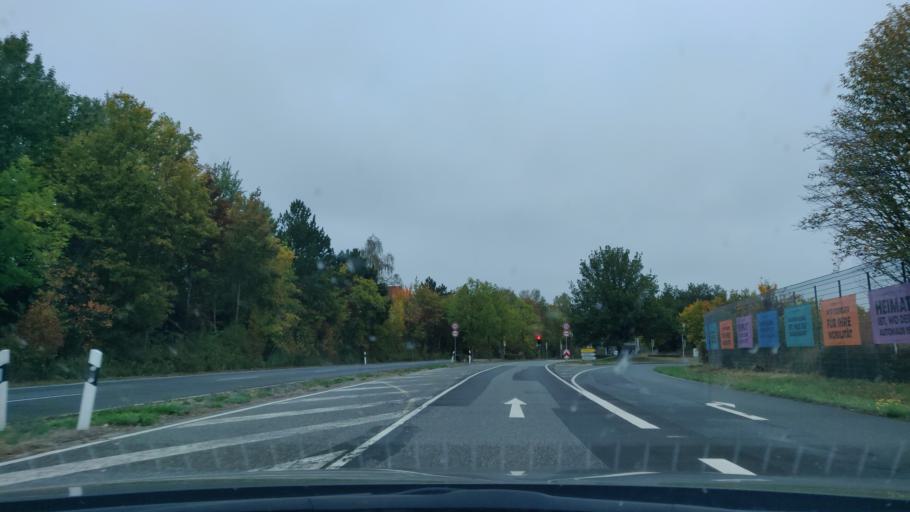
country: DE
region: Hesse
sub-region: Regierungsbezirk Kassel
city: Baunatal
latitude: 51.2622
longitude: 9.4233
